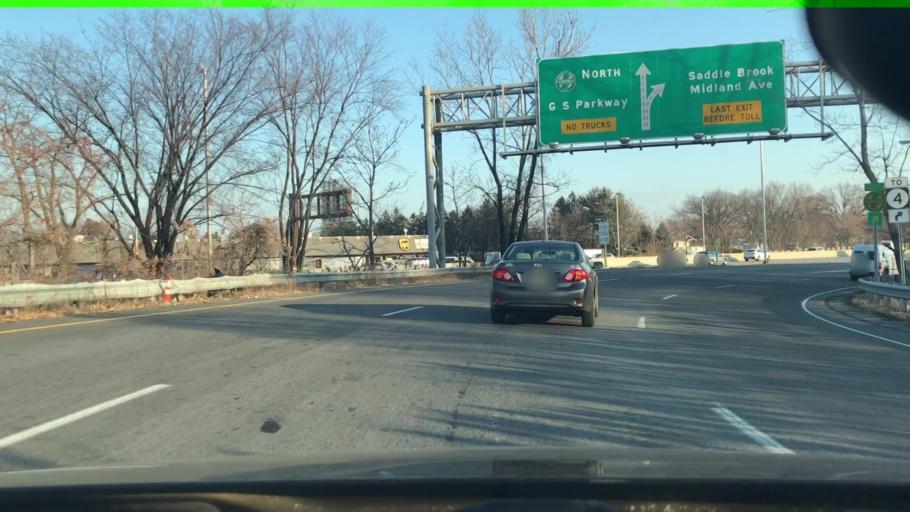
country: US
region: New Jersey
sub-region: Bergen County
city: Saddle Brook
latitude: 40.9068
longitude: -74.1005
